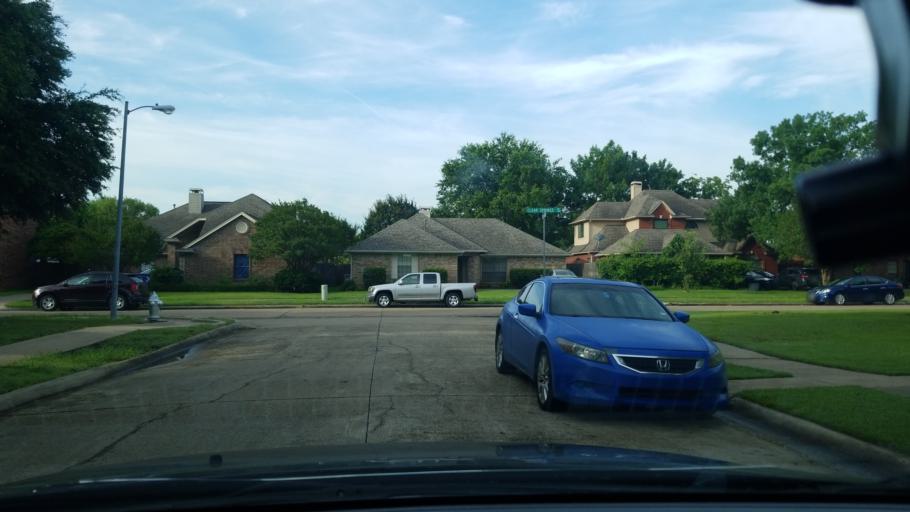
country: US
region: Texas
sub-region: Dallas County
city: Mesquite
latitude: 32.8002
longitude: -96.6012
